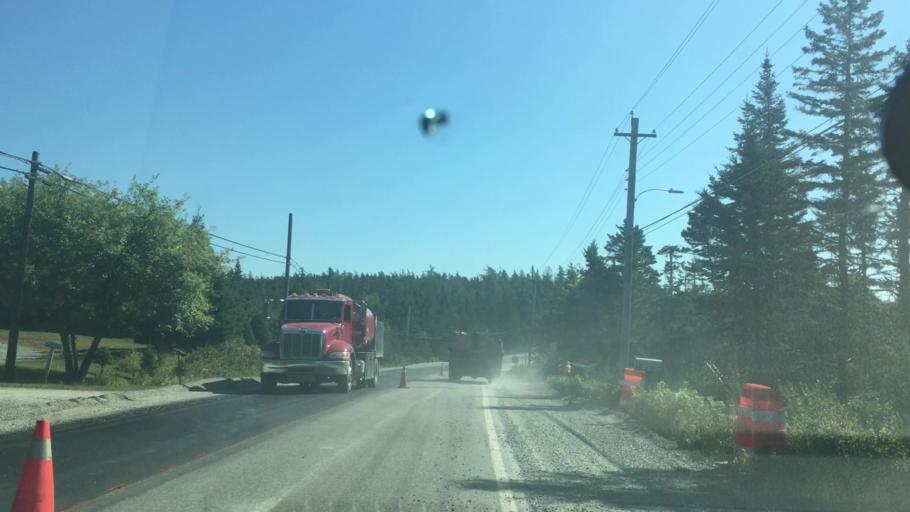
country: CA
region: Nova Scotia
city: New Glasgow
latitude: 44.9071
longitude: -62.4941
